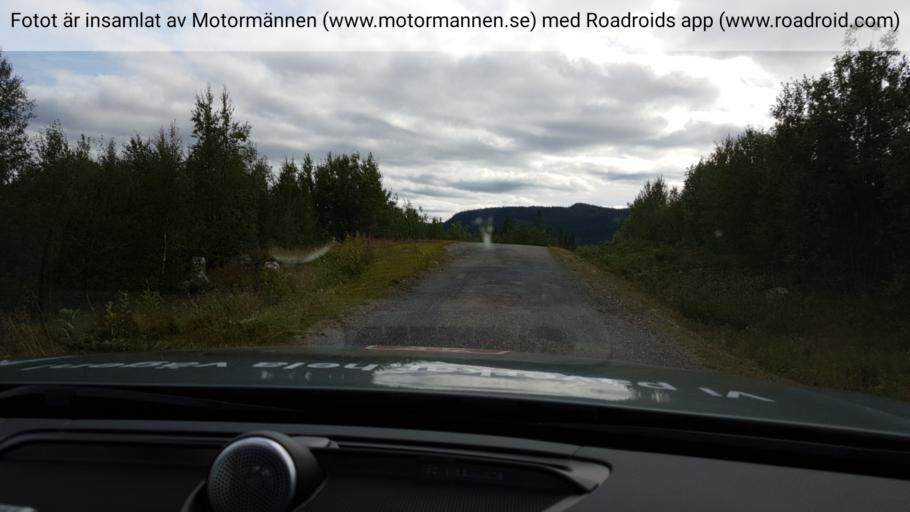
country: SE
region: Jaemtland
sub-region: Stroemsunds Kommun
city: Stroemsund
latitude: 64.5420
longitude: 15.3044
